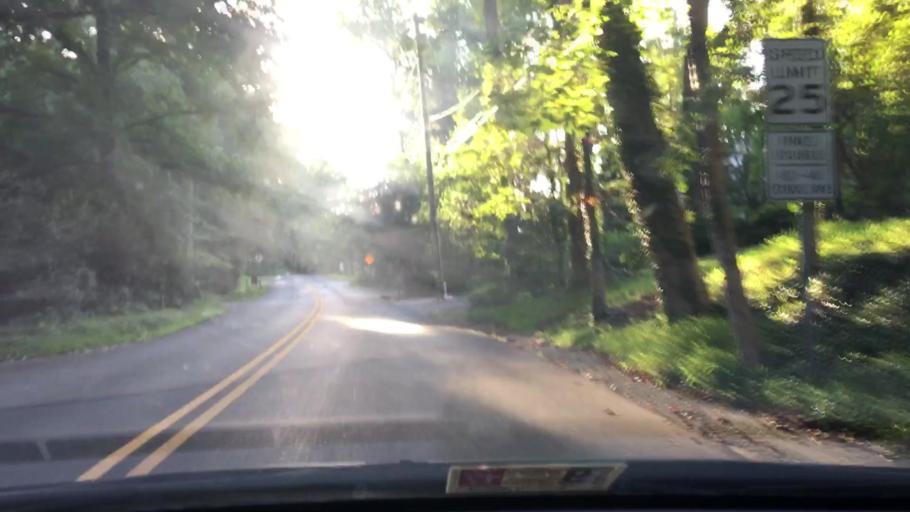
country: US
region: Maryland
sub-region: Montgomery County
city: Cabin John
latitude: 39.0078
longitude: -77.1367
